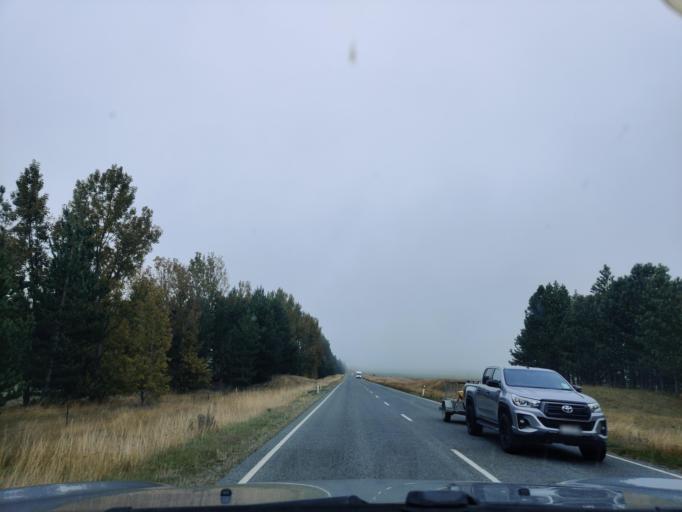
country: NZ
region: Canterbury
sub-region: Timaru District
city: Pleasant Point
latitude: -44.1861
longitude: 170.3049
